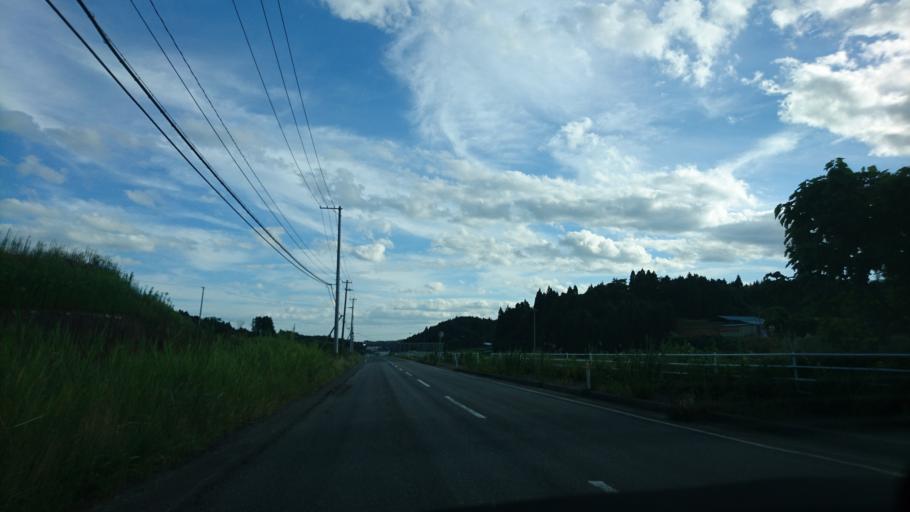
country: JP
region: Iwate
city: Ichinoseki
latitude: 38.8612
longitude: 141.1853
